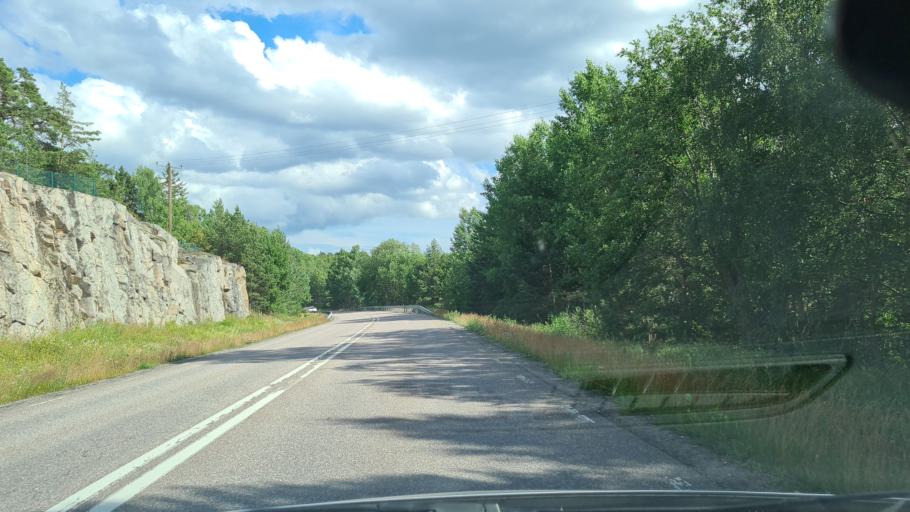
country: SE
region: Stockholm
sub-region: Vaxholms Kommun
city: Vaxholm
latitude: 59.3946
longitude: 18.4058
